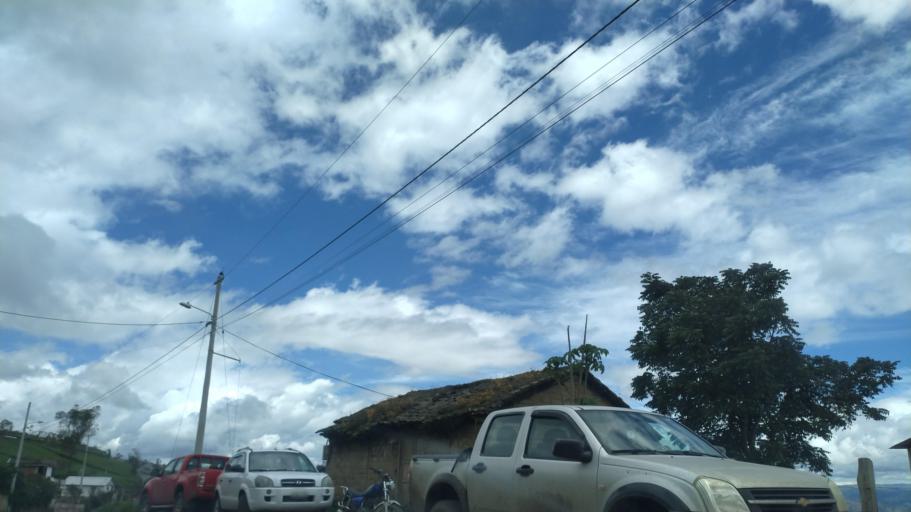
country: EC
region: Chimborazo
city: Riobamba
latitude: -1.6761
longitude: -78.5724
